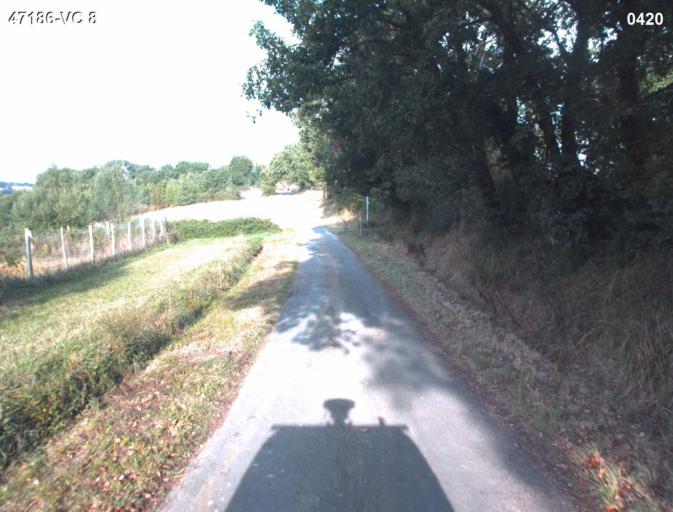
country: FR
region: Aquitaine
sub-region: Departement du Lot-et-Garonne
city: Port-Sainte-Marie
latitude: 44.1841
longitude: 0.4276
